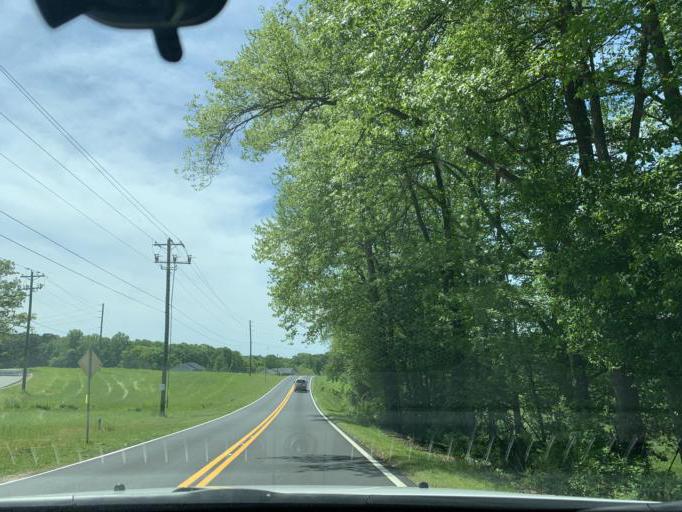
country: US
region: Georgia
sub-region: Forsyth County
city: Cumming
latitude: 34.2644
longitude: -84.0482
